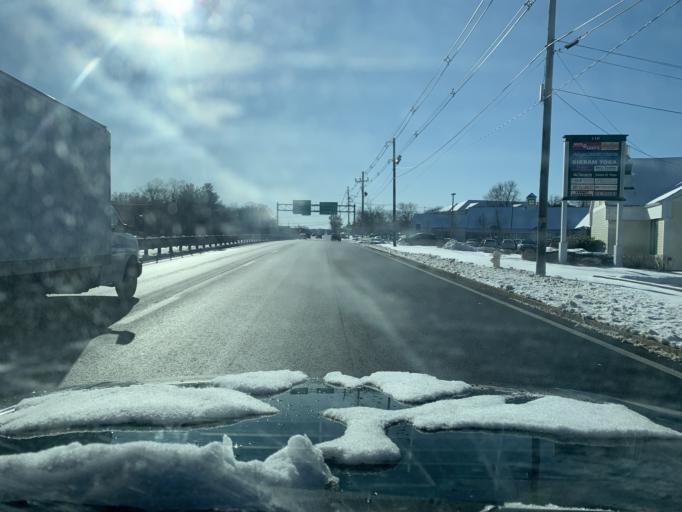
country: US
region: Massachusetts
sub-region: Essex County
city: Danvers
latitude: 42.5688
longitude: -70.9740
